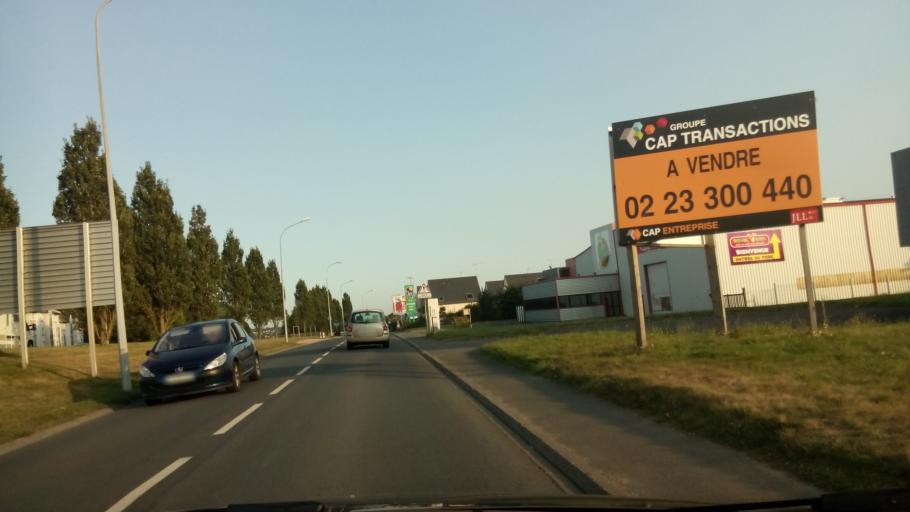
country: FR
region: Brittany
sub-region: Departement des Cotes-d'Armor
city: Lannion
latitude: 48.7442
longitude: -3.4754
